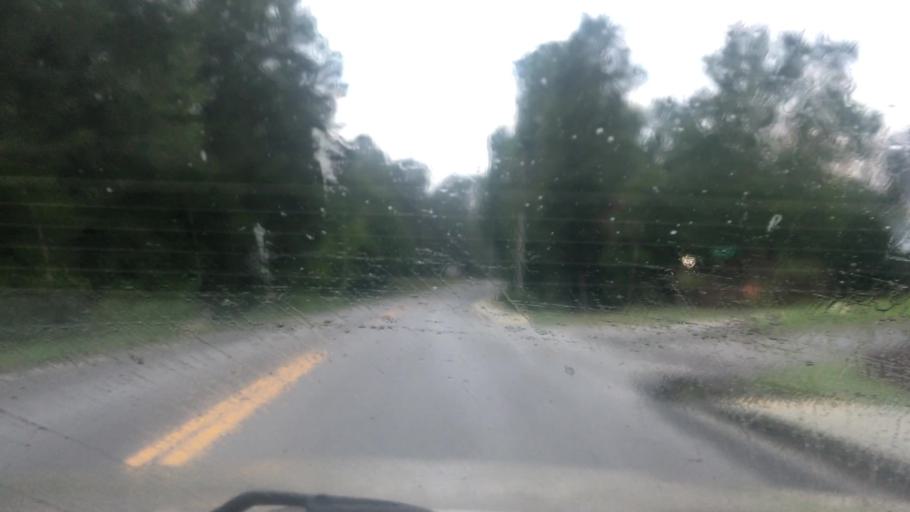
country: US
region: South Carolina
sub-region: Lexington County
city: Irmo
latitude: 34.1481
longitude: -81.1979
